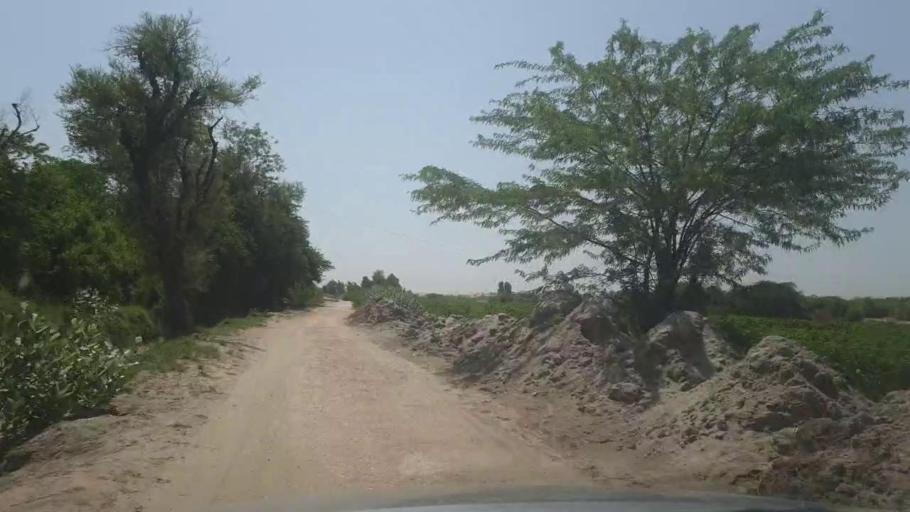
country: PK
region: Sindh
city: Khairpur
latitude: 27.3530
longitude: 69.0441
